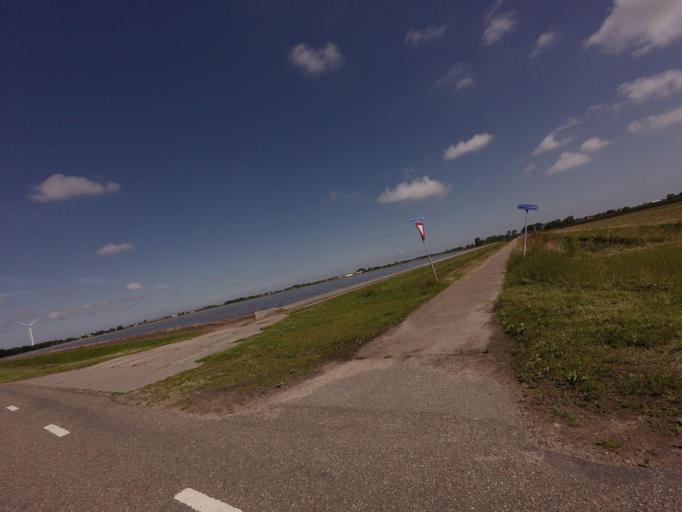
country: NL
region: North Holland
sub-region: Gemeente Schagen
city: Schagen
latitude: 52.8717
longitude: 4.8372
